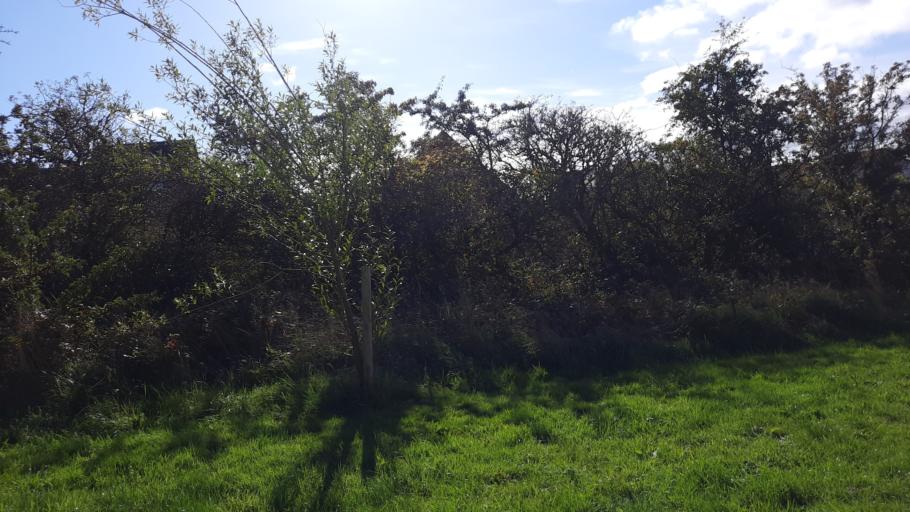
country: GB
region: England
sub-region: Gateshead
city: Lamesley
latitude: 54.9049
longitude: -1.5703
